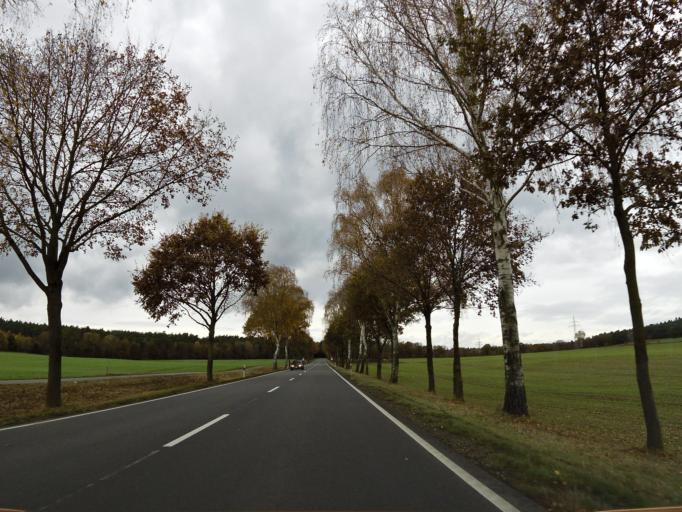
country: DE
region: Lower Saxony
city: Schnega
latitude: 52.9147
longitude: 10.8905
